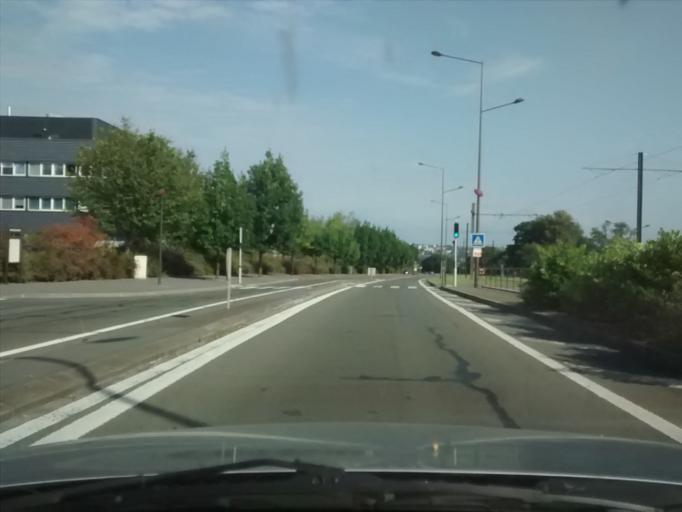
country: FR
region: Pays de la Loire
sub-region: Departement de la Sarthe
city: La Chapelle-Saint-Aubin
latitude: 48.0200
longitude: 0.1626
